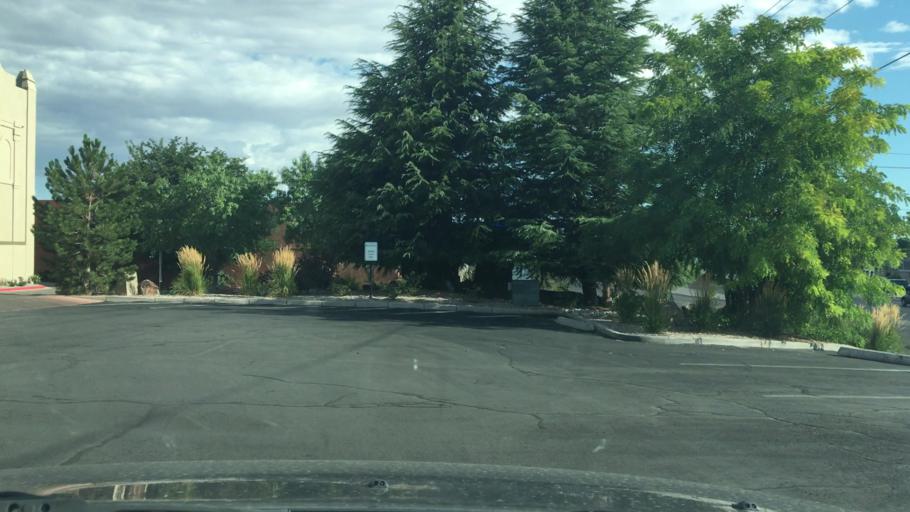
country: US
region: New Mexico
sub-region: Bernalillo County
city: Albuquerque
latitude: 35.1077
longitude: -106.6039
